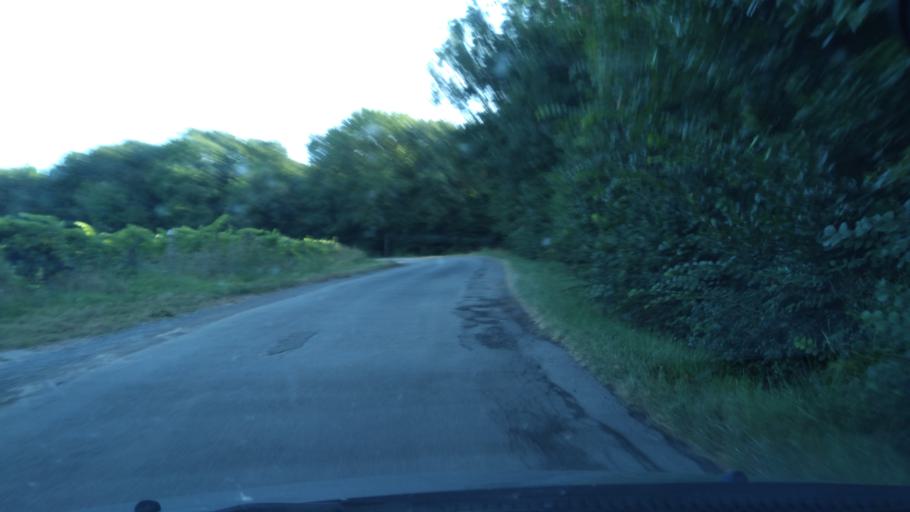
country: FR
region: Poitou-Charentes
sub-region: Departement de la Charente-Maritime
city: Dolus-d'Oleron
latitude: 45.9469
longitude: -1.3462
